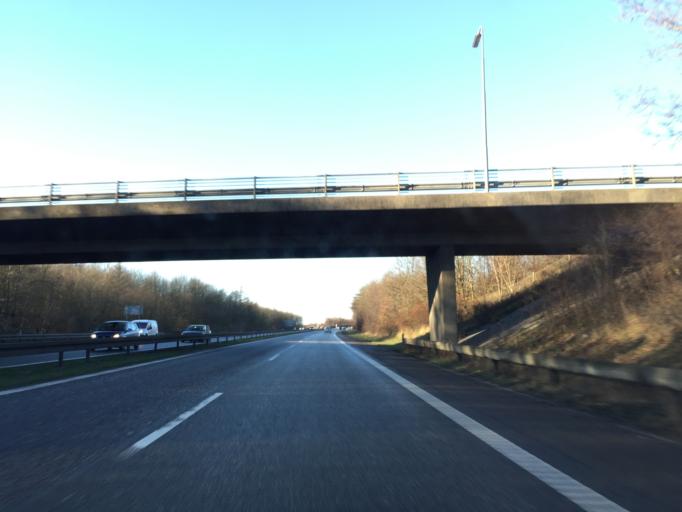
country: DK
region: South Denmark
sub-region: Odense Kommune
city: Bellinge
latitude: 55.3638
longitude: 10.3272
